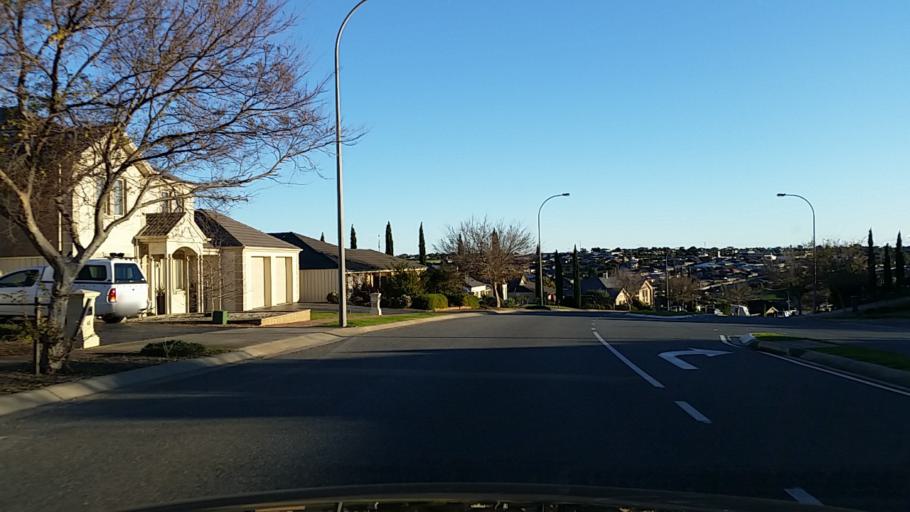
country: AU
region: South Australia
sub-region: Onkaparinga
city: Moana
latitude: -35.2093
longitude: 138.4876
